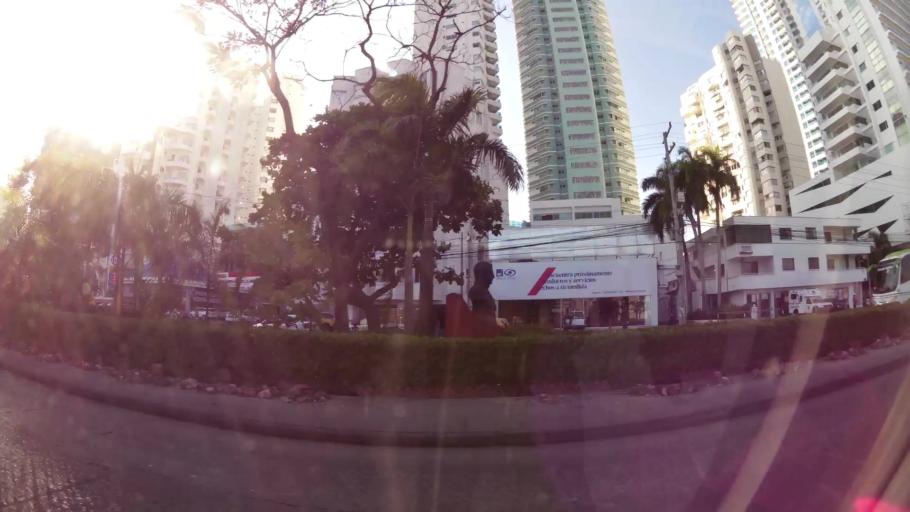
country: CO
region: Bolivar
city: Cartagena
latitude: 10.4078
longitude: -75.5511
